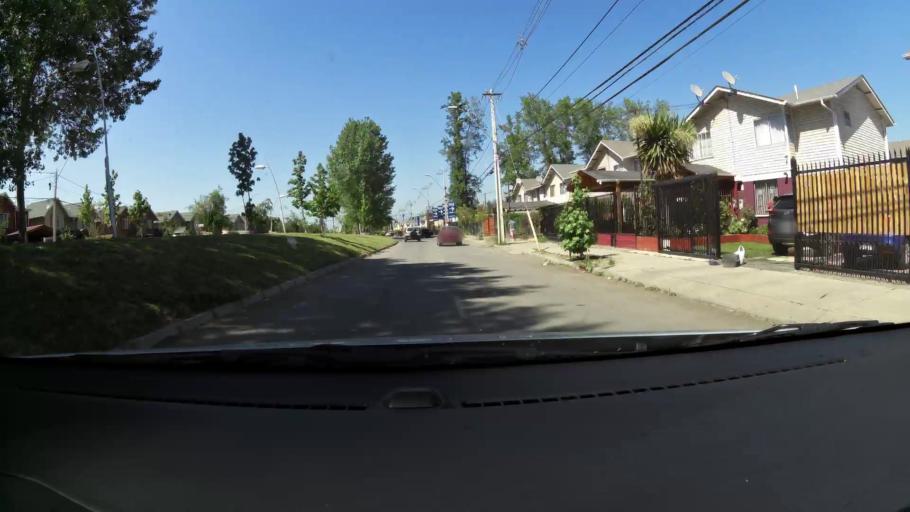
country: CL
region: Santiago Metropolitan
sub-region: Provincia de Maipo
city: San Bernardo
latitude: -33.6114
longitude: -70.6877
